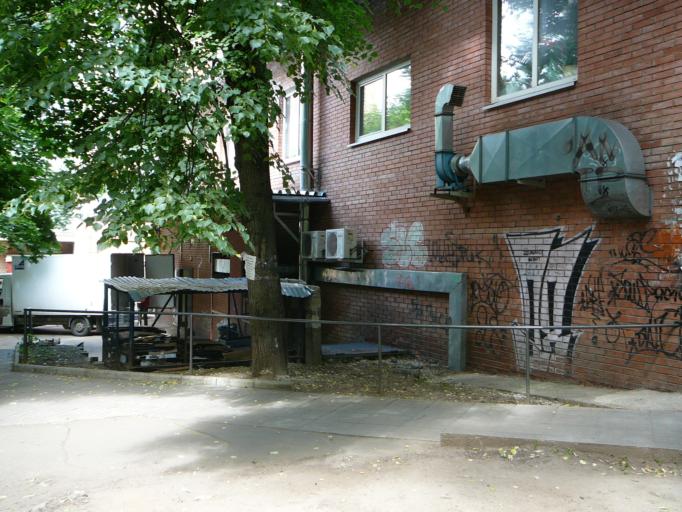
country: RU
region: Moskovskaya
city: Krasnogorsk
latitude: 55.8168
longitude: 37.3169
